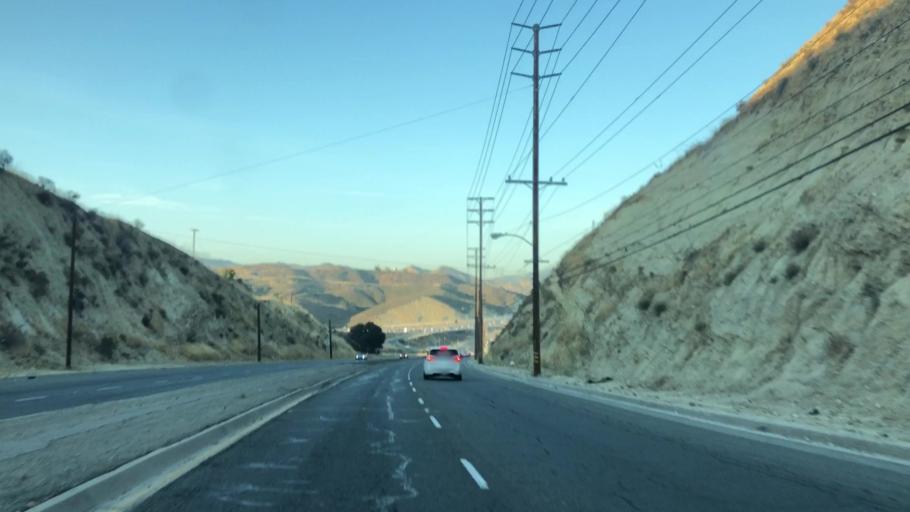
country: US
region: California
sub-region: Los Angeles County
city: Santa Clarita
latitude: 34.3857
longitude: -118.4904
